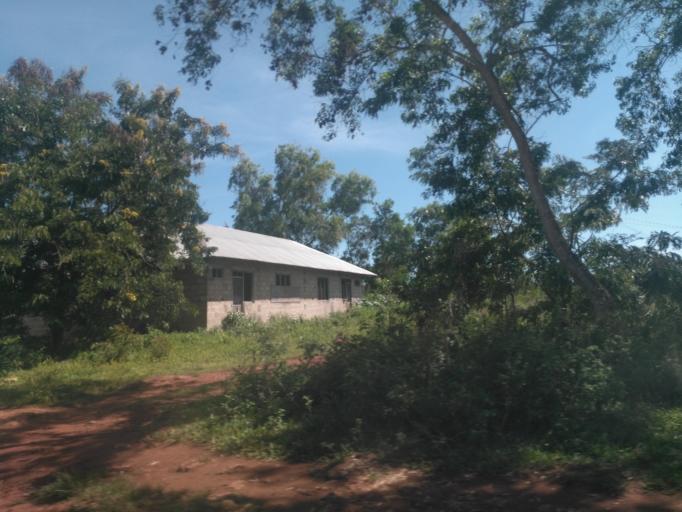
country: TZ
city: Kiwengwa
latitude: -5.9851
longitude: 39.3312
